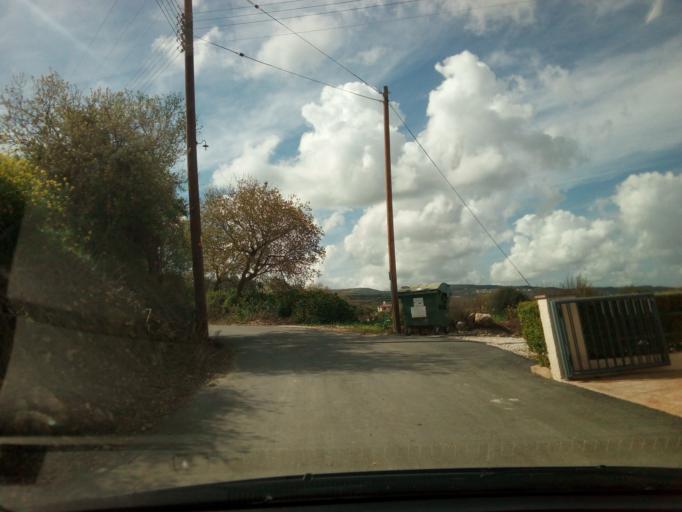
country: CY
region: Pafos
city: Tala
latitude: 34.8926
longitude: 32.4826
